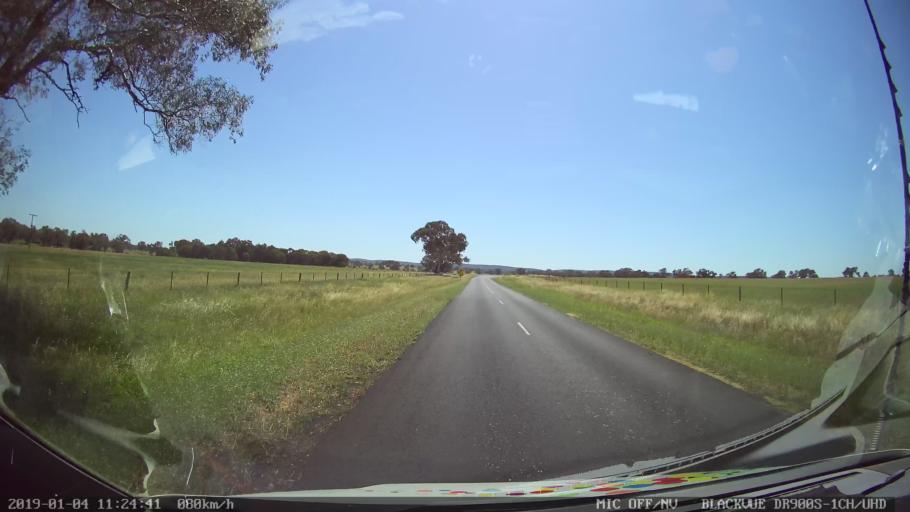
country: AU
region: New South Wales
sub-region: Cabonne
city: Molong
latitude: -33.1311
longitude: 148.7501
